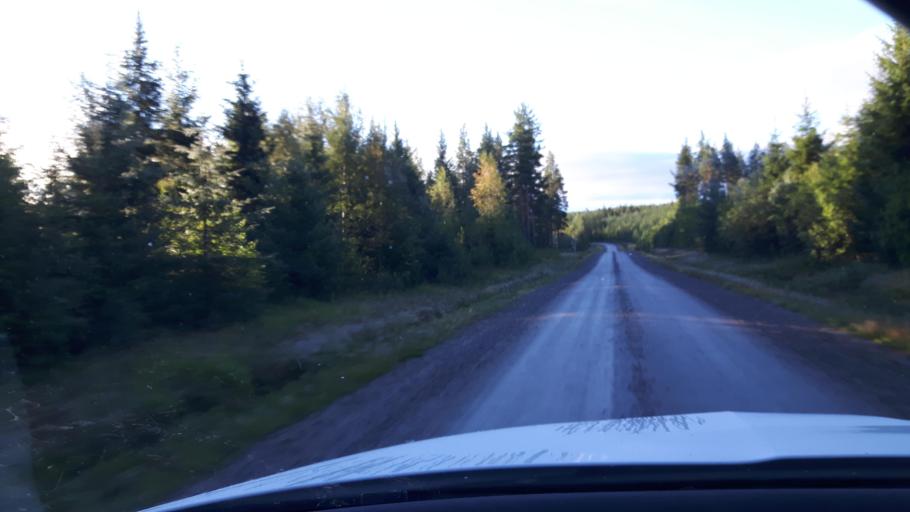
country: SE
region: Gaevleborg
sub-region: Ljusdals Kommun
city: Farila
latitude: 62.1171
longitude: 15.6866
